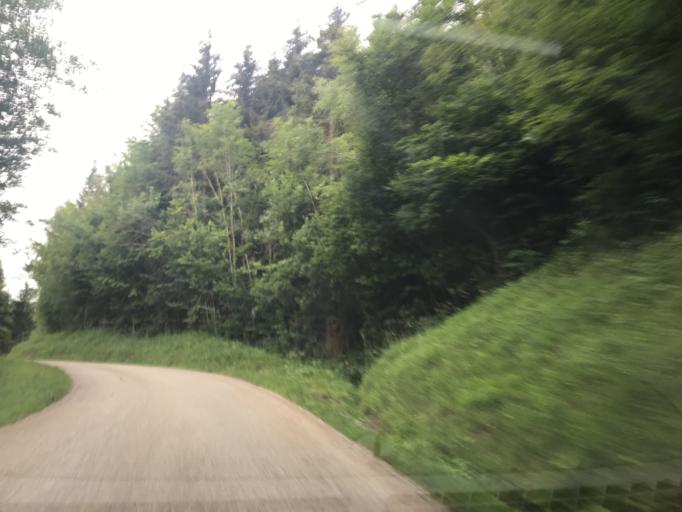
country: FR
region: Rhone-Alpes
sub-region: Departement de l'Isere
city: Le Touvet
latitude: 45.3652
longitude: 5.9200
